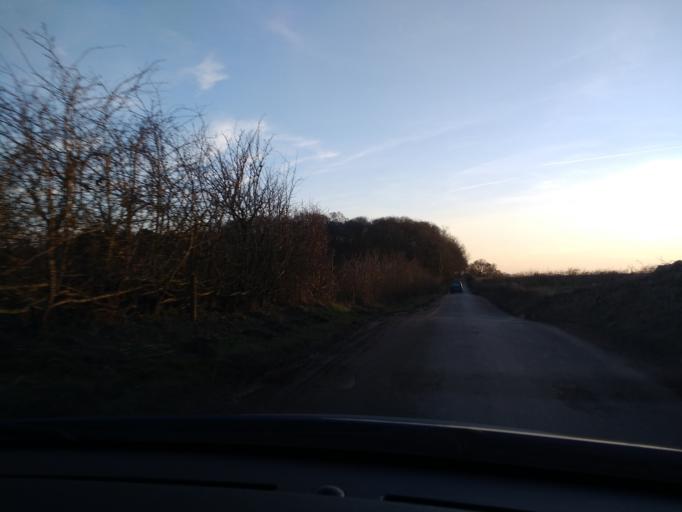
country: GB
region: England
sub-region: Cumbria
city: Appleby-in-Westmorland
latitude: 54.6065
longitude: -2.4868
